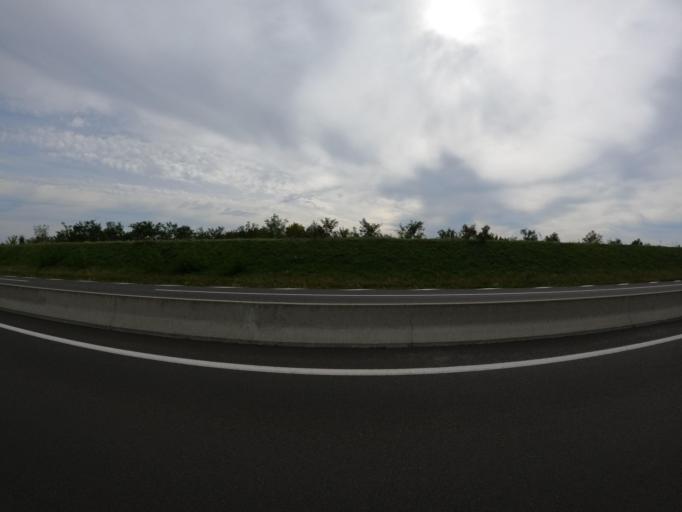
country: FR
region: Auvergne
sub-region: Departement de l'Allier
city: Souvigny
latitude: 46.4562
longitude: 3.2385
